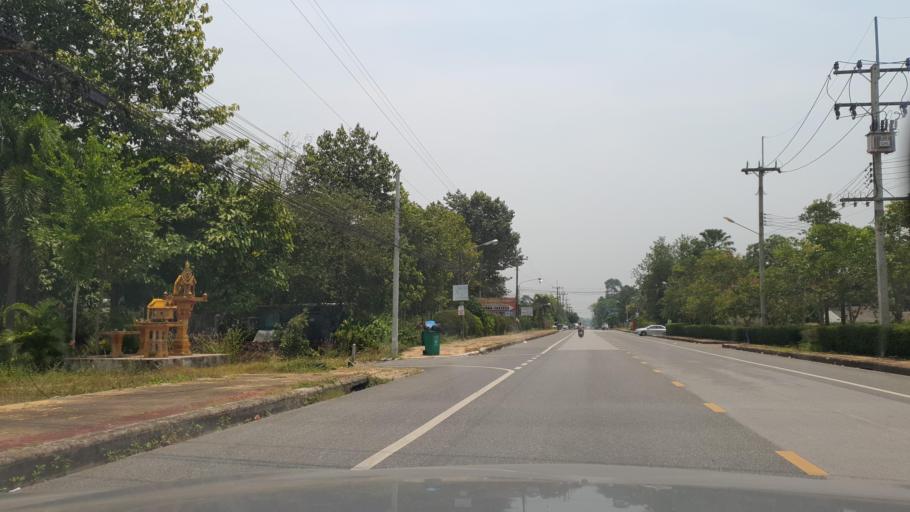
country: TH
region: Rayong
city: Nikhom Phattana
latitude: 12.7863
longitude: 101.1660
